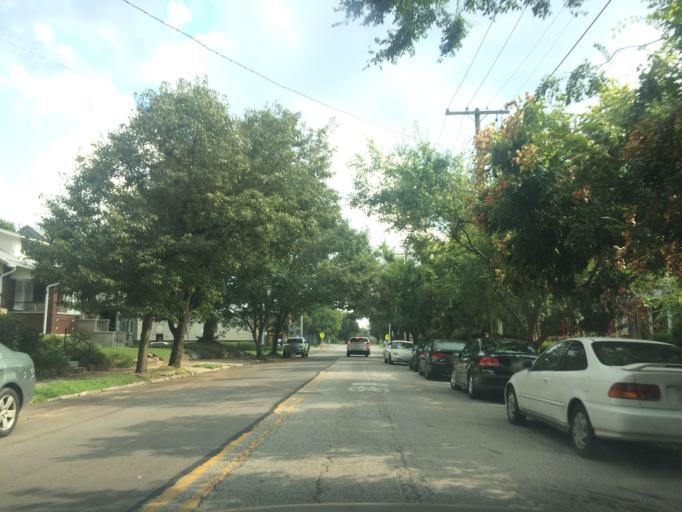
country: US
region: Kentucky
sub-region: Jefferson County
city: Louisville
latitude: 38.2265
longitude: -85.7568
